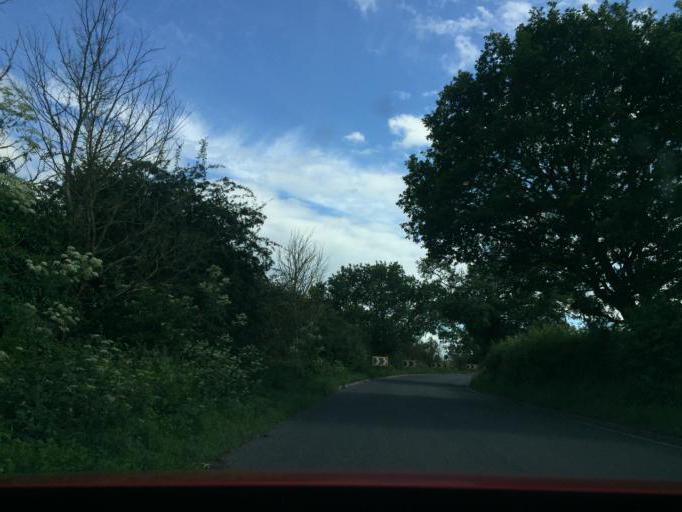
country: GB
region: England
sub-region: Hertfordshire
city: Codicote
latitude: 51.8609
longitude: -0.2354
